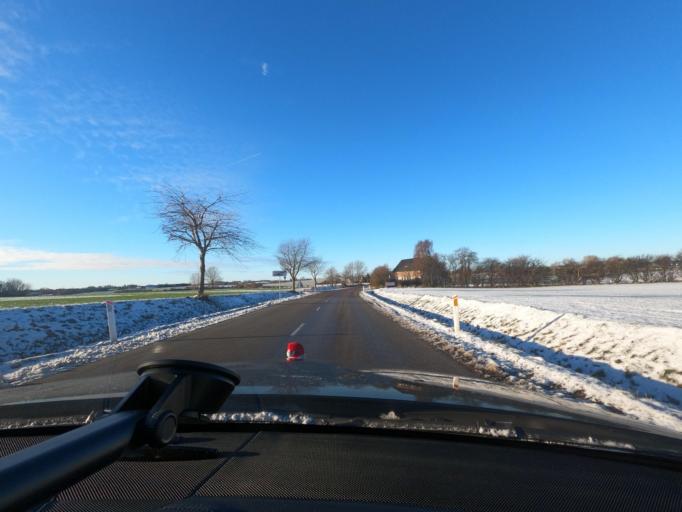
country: DK
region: South Denmark
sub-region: Sonderborg Kommune
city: Horuphav
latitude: 54.8765
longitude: 9.9206
